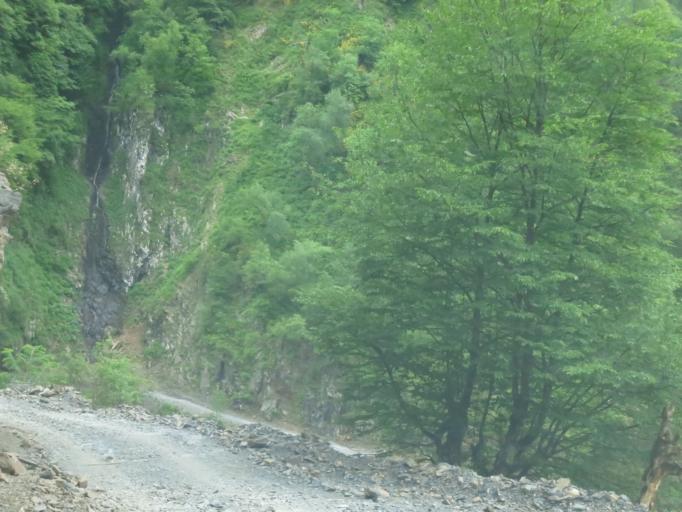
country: GE
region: Kakheti
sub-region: Telavi
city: Telavi
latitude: 42.2459
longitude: 45.4967
